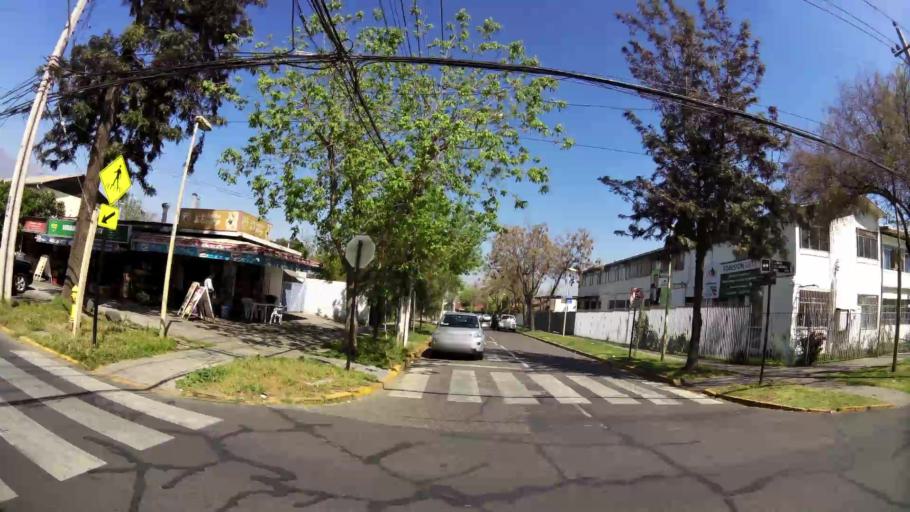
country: CL
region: Santiago Metropolitan
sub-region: Provincia de Santiago
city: Villa Presidente Frei, Nunoa, Santiago, Chile
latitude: -33.4215
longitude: -70.5583
